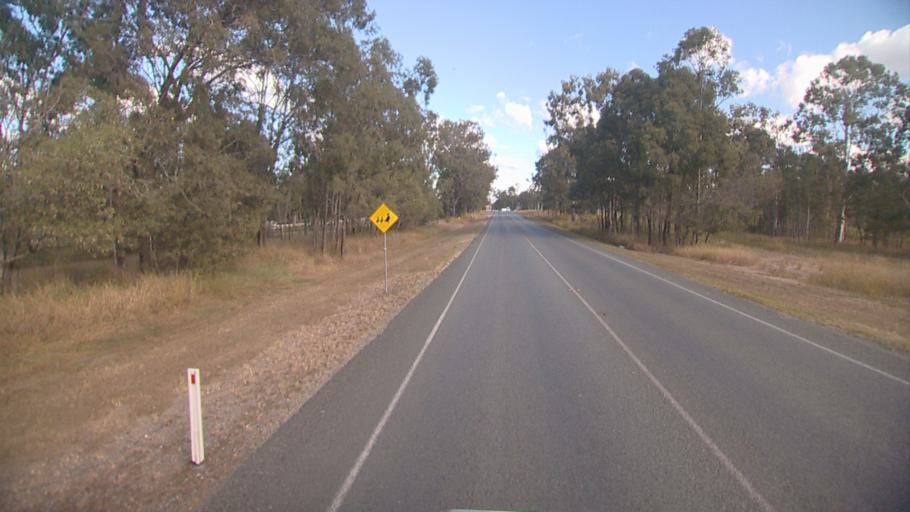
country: AU
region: Queensland
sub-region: Logan
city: Park Ridge South
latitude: -27.7254
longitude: 152.9847
